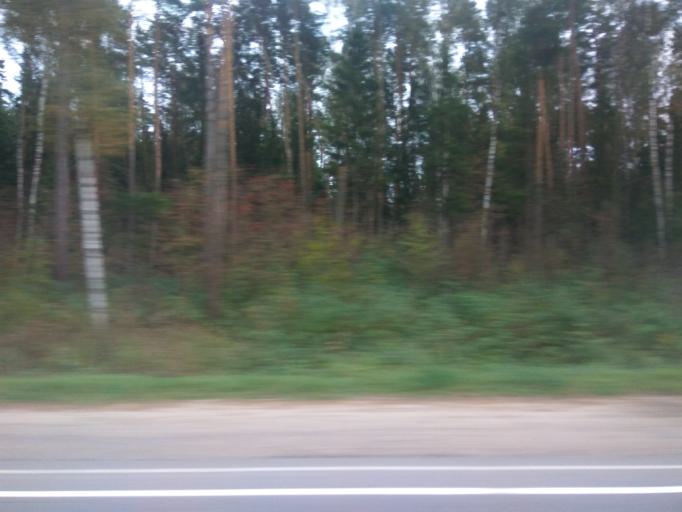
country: RU
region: Moskovskaya
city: Krasnoarmeysk
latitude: 56.0401
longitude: 38.1992
